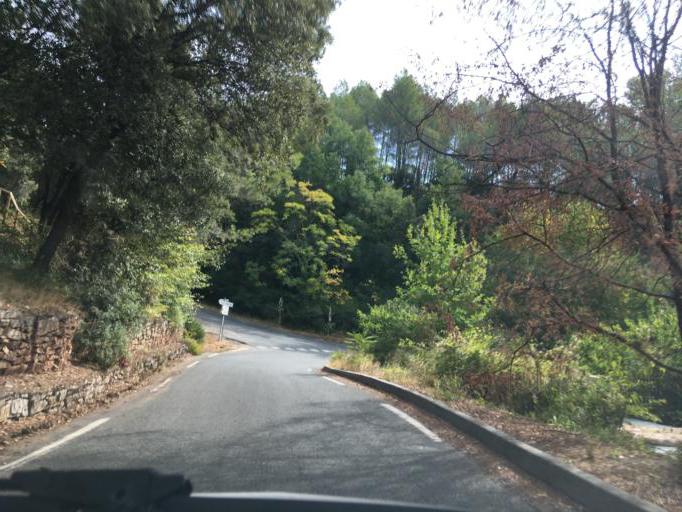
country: FR
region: Provence-Alpes-Cote d'Azur
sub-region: Departement du Var
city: Taradeau
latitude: 43.4552
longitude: 6.4283
